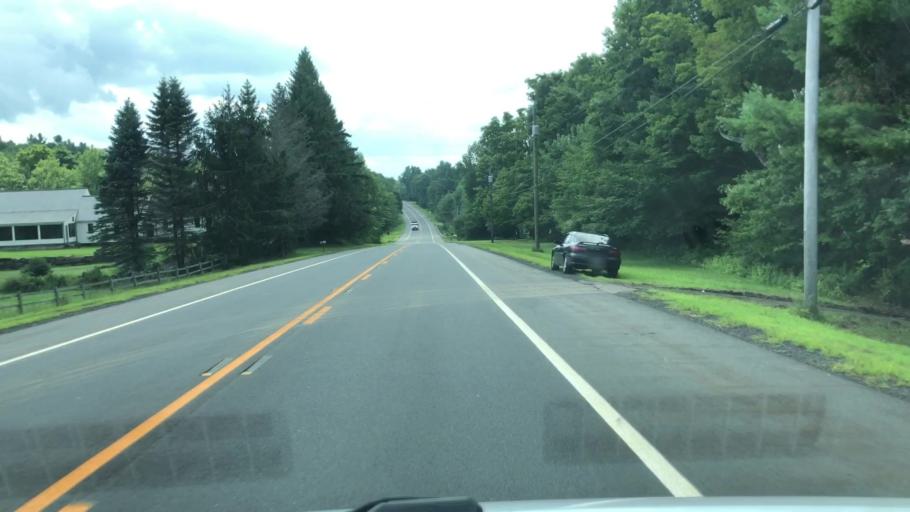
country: US
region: Massachusetts
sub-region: Franklin County
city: Ashfield
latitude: 42.4938
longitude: -72.8081
